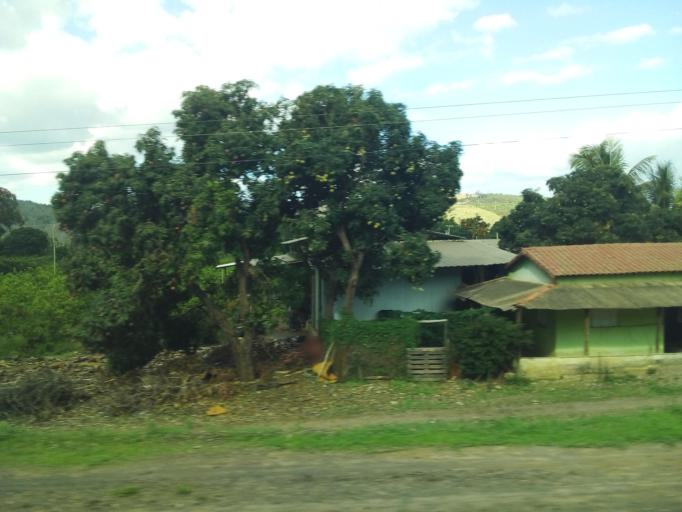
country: BR
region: Minas Gerais
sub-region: Conselheiro Pena
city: Conselheiro Pena
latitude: -19.1155
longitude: -41.5060
